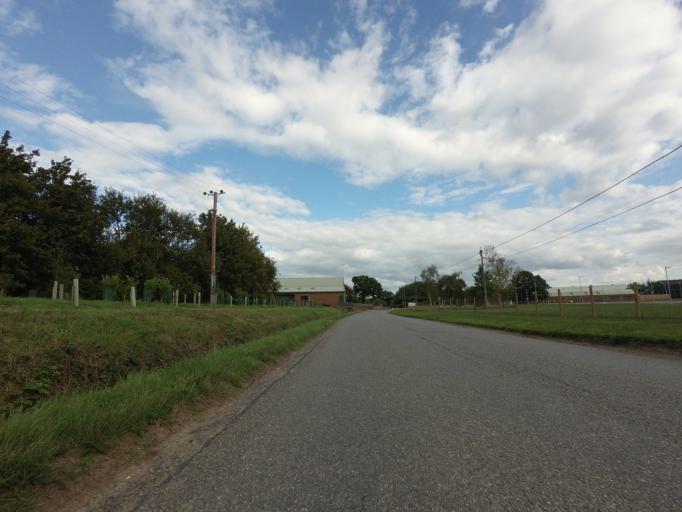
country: GB
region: England
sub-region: Kent
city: Marden
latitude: 51.2123
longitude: 0.4950
